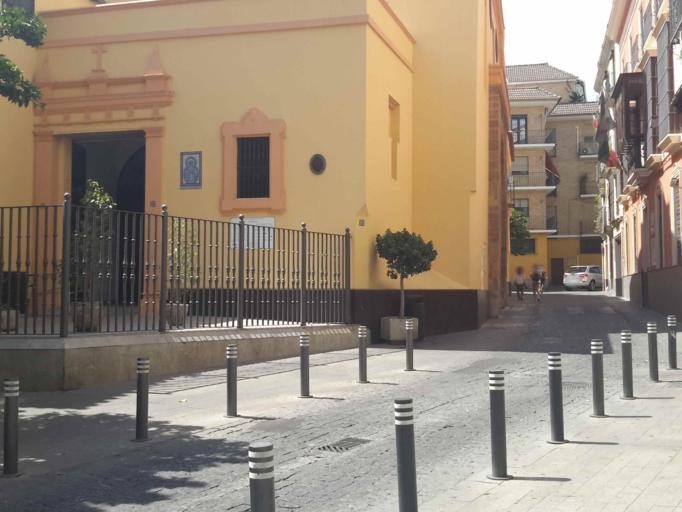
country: ES
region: Andalusia
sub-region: Provincia de Sevilla
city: Sevilla
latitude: 37.3897
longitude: -5.9909
